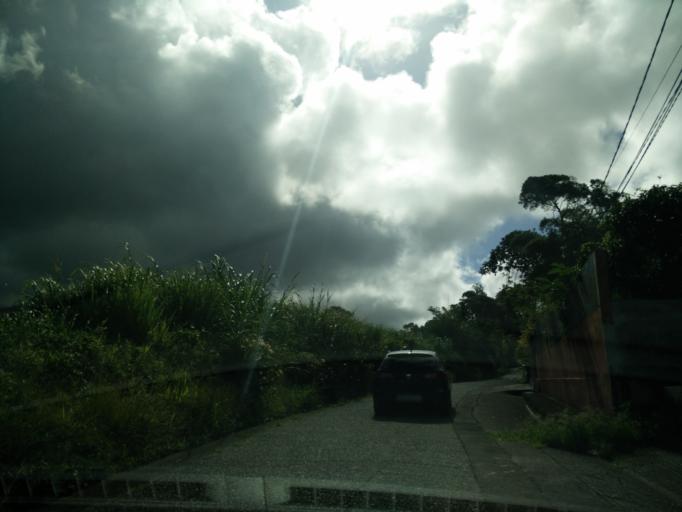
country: MQ
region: Martinique
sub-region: Martinique
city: Basse-Pointe
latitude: 14.8197
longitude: -61.1237
